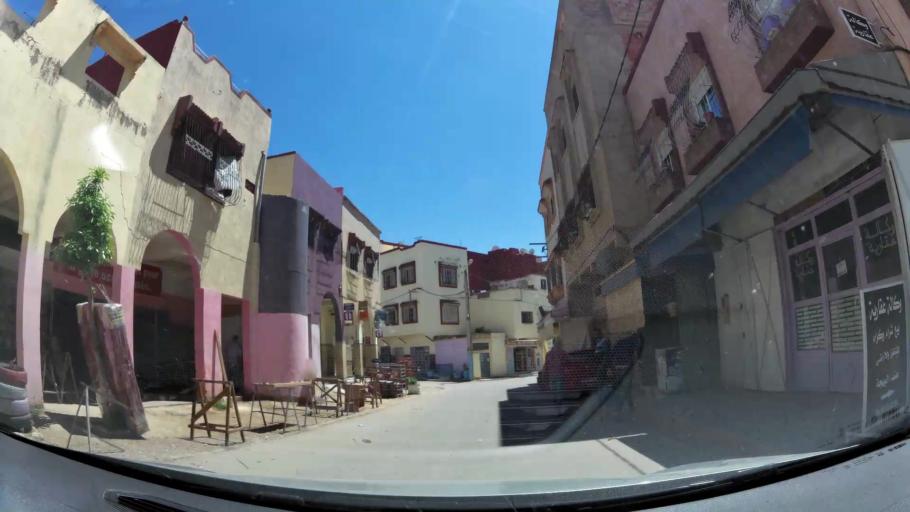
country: MA
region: Meknes-Tafilalet
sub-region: Meknes
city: Meknes
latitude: 33.9020
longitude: -5.5759
